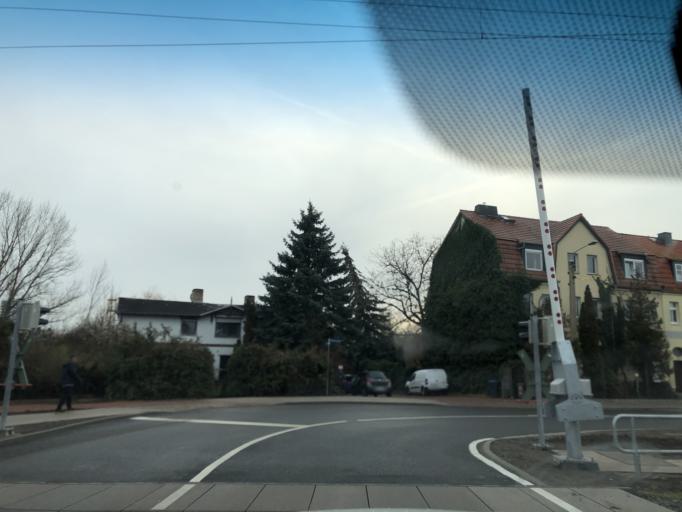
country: DE
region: Saxony-Anhalt
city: Halle Neustadt
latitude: 51.4858
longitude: 11.9151
